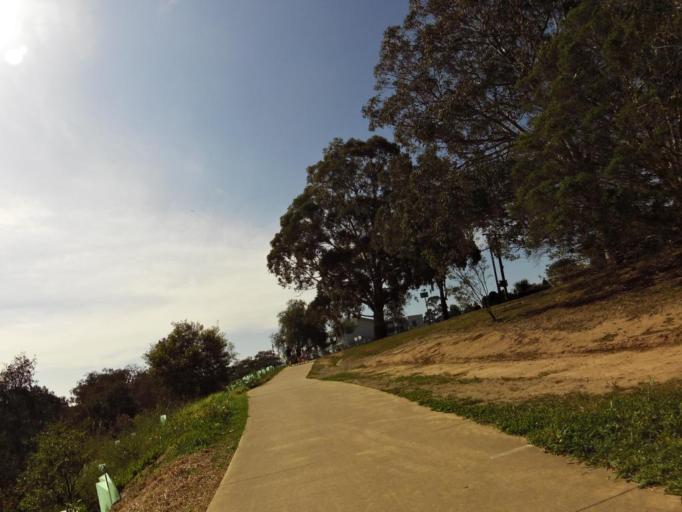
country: AU
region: Victoria
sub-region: Wyndham
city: Werribee
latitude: -37.9083
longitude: 144.6524
